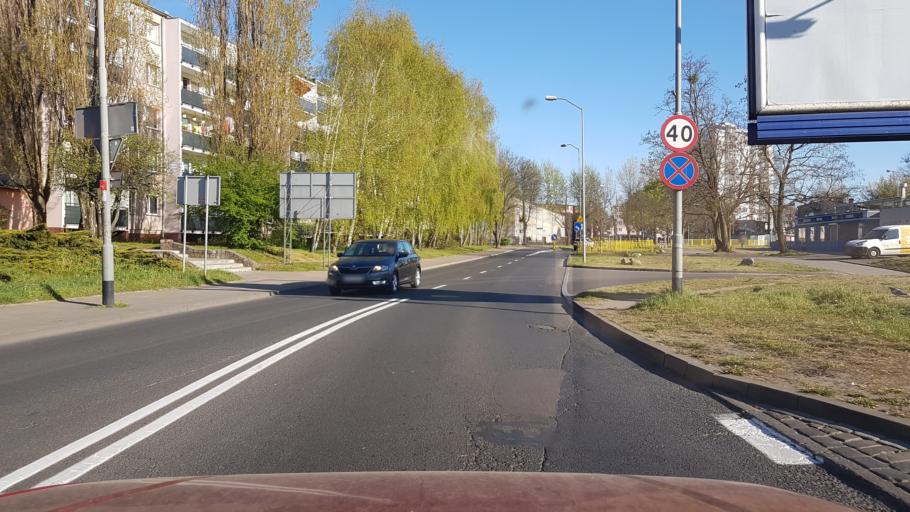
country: PL
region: West Pomeranian Voivodeship
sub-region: Szczecin
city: Szczecin
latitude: 53.3827
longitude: 14.6344
